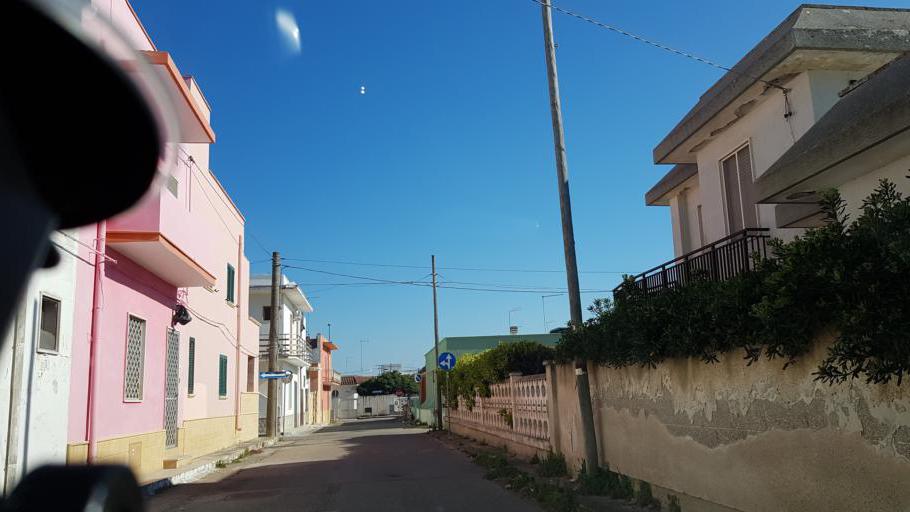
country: IT
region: Apulia
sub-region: Provincia di Brindisi
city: Torchiarolo
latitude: 40.5197
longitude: 18.0879
